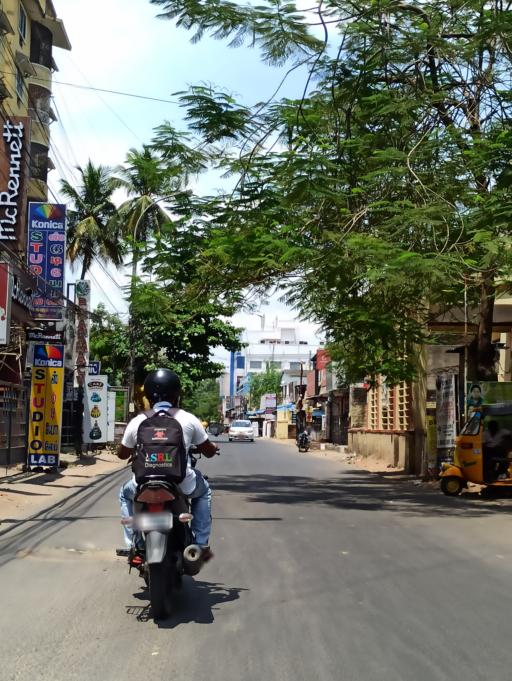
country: IN
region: Tamil Nadu
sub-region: Chennai
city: Chetput
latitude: 13.0658
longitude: 80.2310
